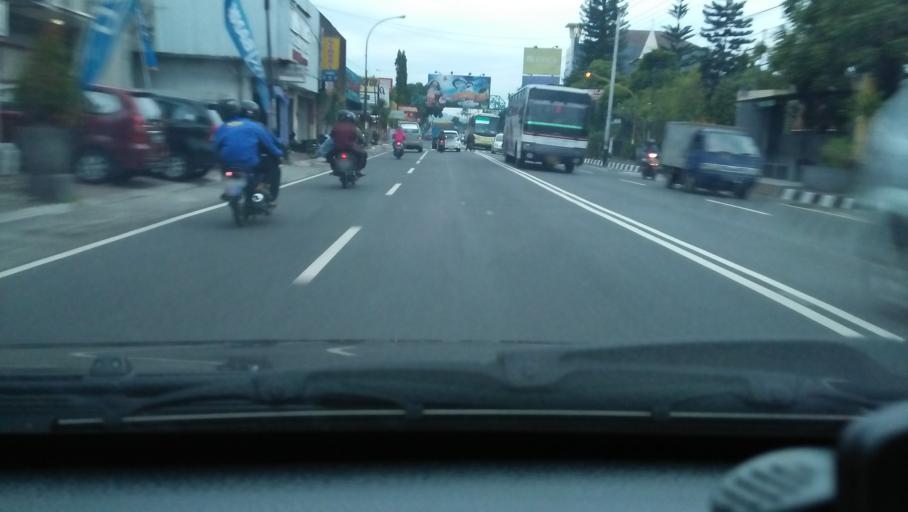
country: ID
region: Central Java
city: Magelang
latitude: -7.4549
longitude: 110.2232
